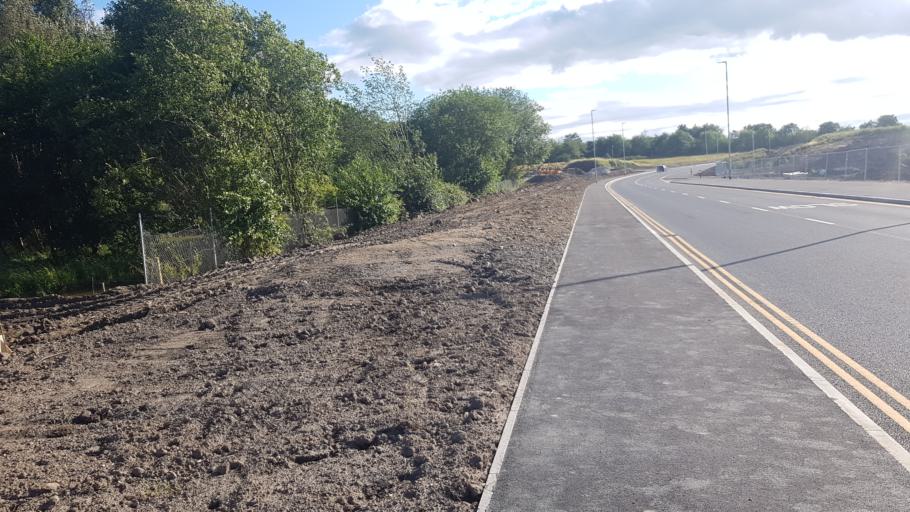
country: GB
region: England
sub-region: City and Borough of Wakefield
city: Castleford
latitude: 53.7068
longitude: -1.3553
